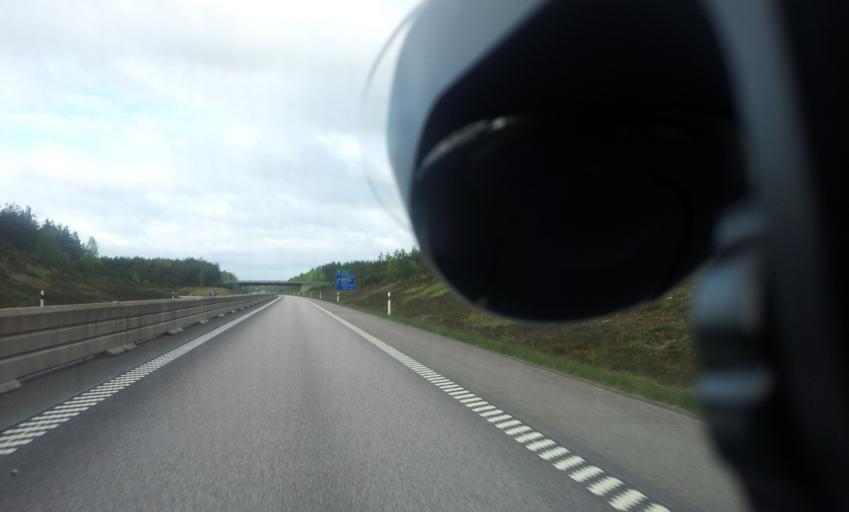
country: SE
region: Kalmar
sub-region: Kalmar Kommun
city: Ljungbyholm
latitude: 56.5970
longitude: 16.1270
